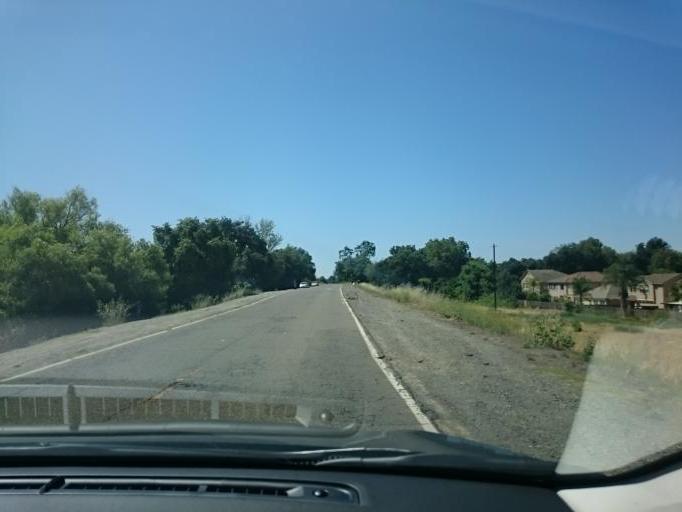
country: US
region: California
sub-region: Yolo County
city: West Sacramento
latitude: 38.5531
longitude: -121.5153
